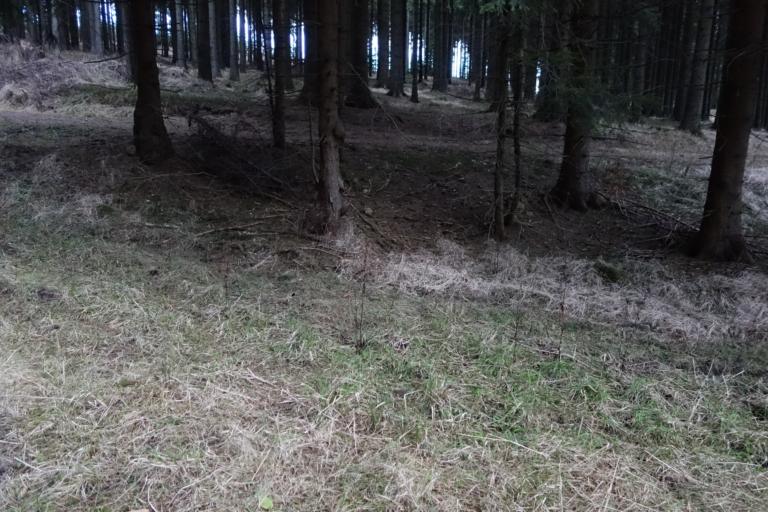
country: DE
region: Saxony
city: Frauenstein
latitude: 50.7802
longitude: 13.6062
